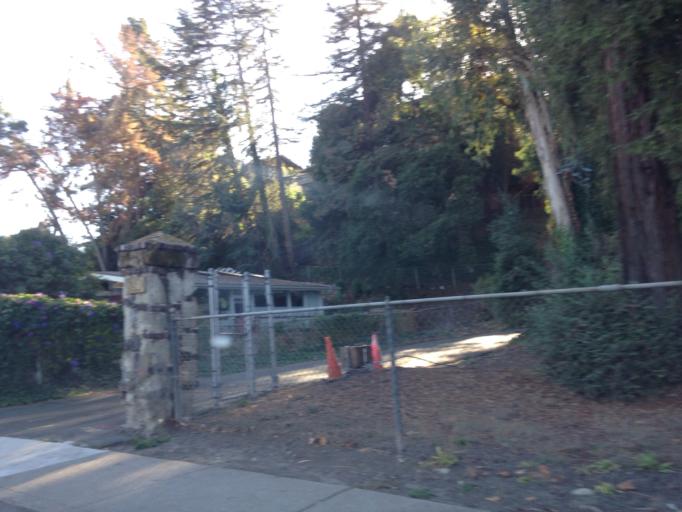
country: US
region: California
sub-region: Contra Costa County
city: Pinole
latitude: 38.0078
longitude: -122.2925
